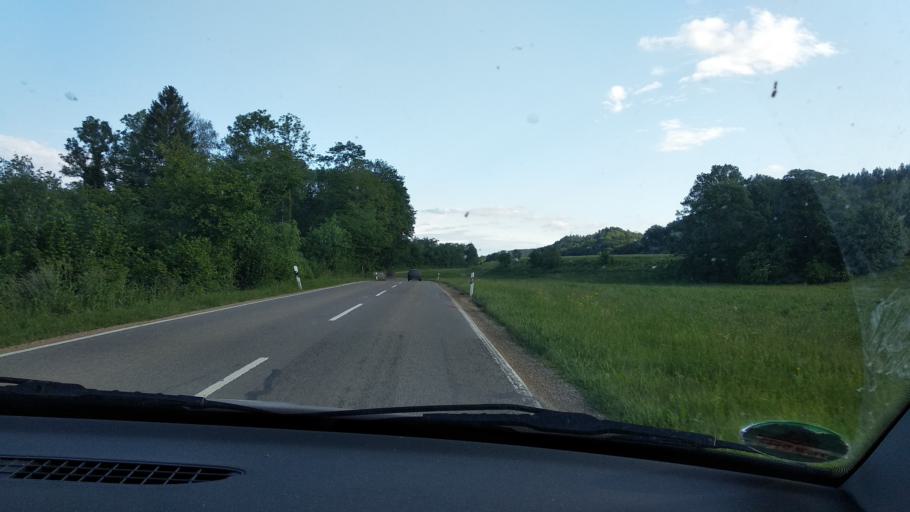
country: DE
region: Baden-Wuerttemberg
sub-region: Tuebingen Region
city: Aitrach
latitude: 47.9610
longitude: 10.0823
